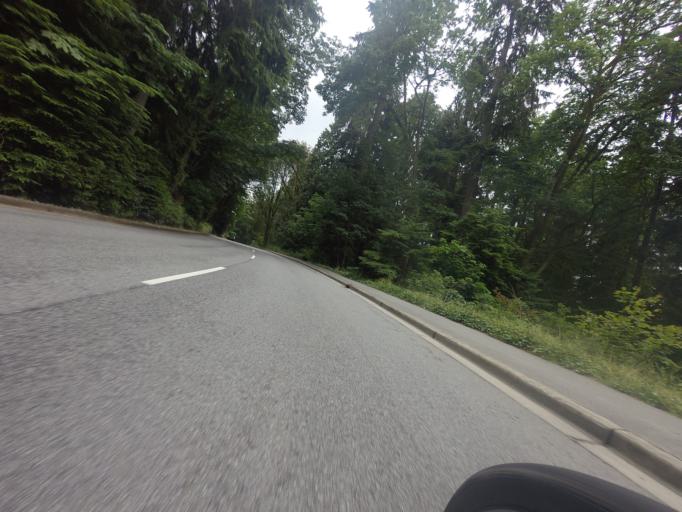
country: CA
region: British Columbia
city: West End
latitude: 49.3081
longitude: -123.1532
